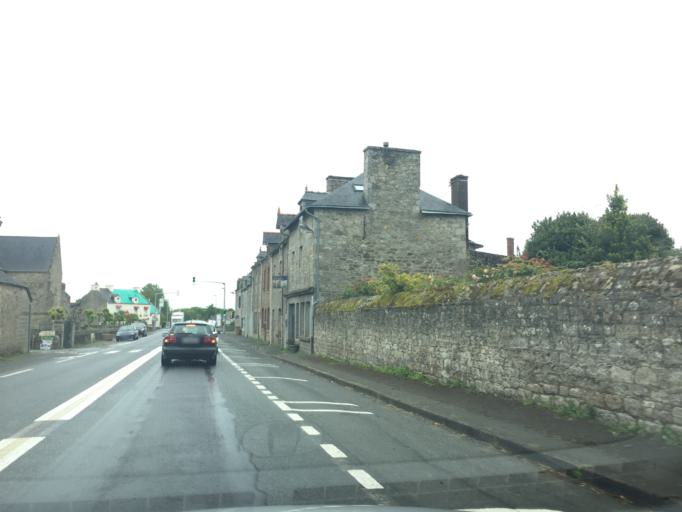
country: FR
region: Brittany
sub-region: Departement des Cotes-d'Armor
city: Crehen
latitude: 48.5689
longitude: -2.1837
